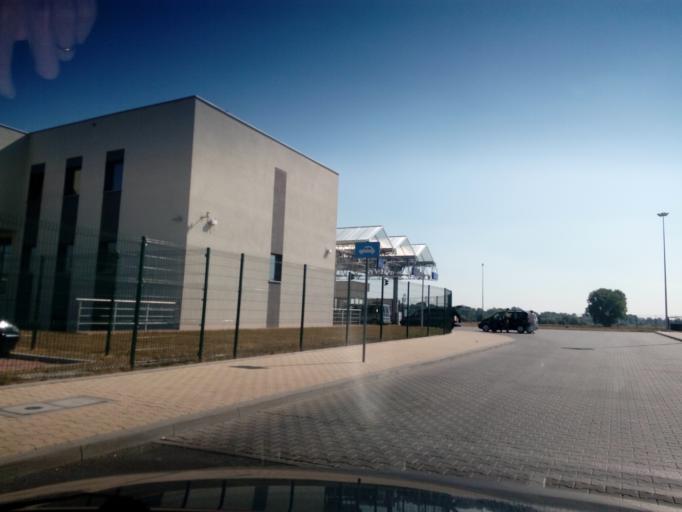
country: PL
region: Lublin Voivodeship
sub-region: Powiat hrubieszowski
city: Horodlo
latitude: 50.8593
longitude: 24.1340
